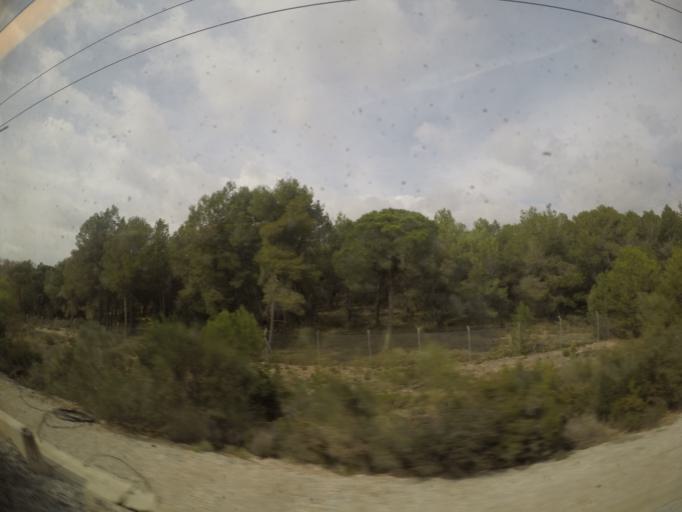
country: ES
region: Catalonia
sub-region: Provincia de Tarragona
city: Santa Oliva
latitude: 41.2591
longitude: 1.5829
